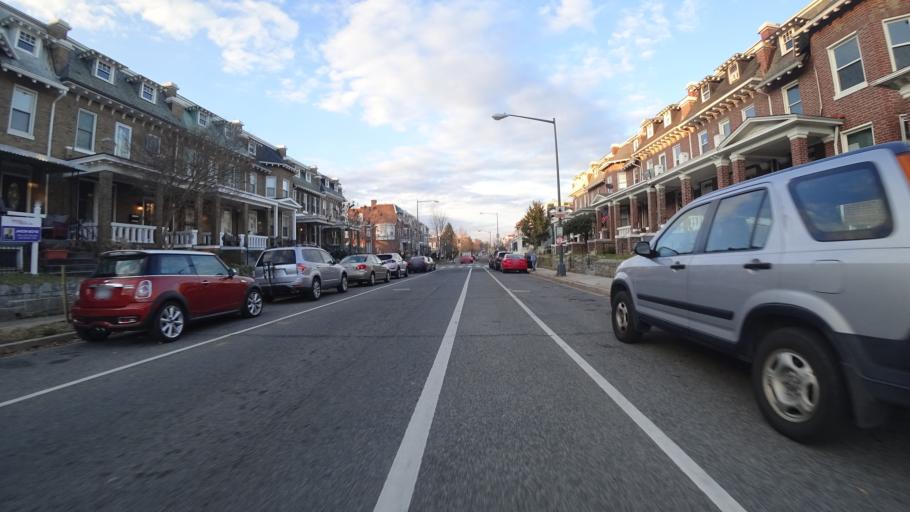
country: US
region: Maryland
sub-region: Prince George's County
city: Chillum
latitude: 38.9358
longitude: -77.0212
